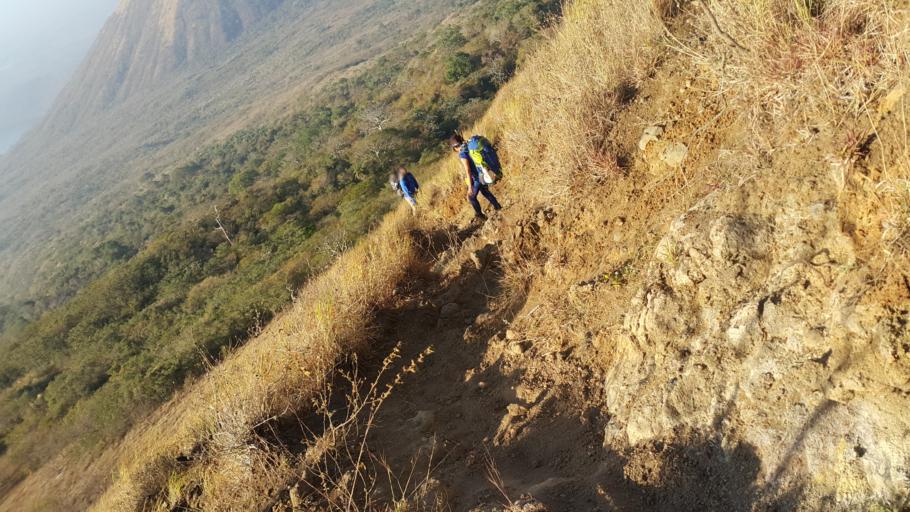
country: NI
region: Leon
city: La Paz Centro
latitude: 12.4839
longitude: -86.6674
